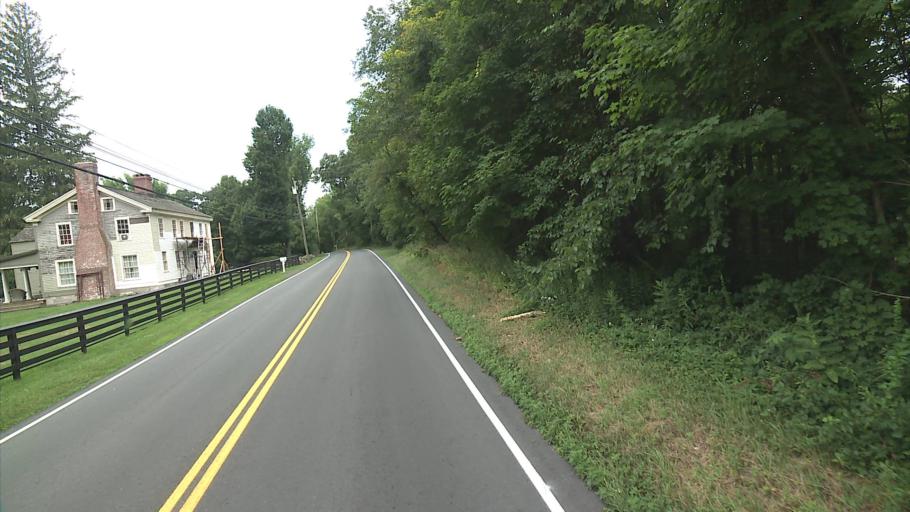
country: US
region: Connecticut
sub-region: New Haven County
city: Heritage Village
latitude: 41.5504
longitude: -73.2967
